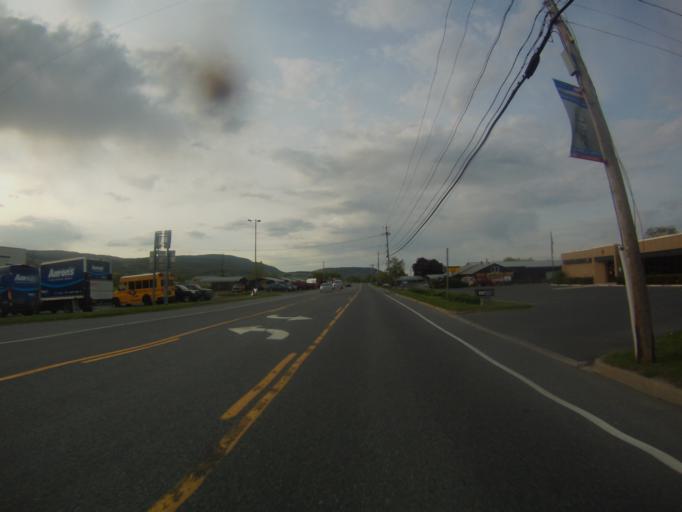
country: US
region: New York
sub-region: Essex County
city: Ticonderoga
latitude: 43.8598
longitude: -73.4378
